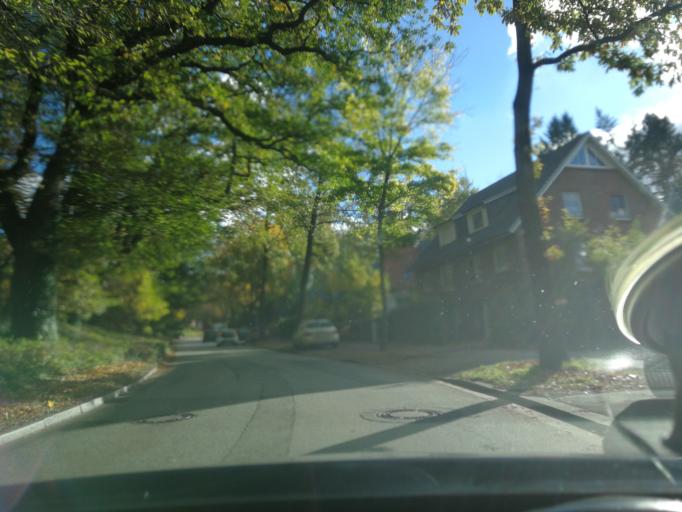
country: DE
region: Hamburg
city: Harburg
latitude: 53.4657
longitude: 9.9535
